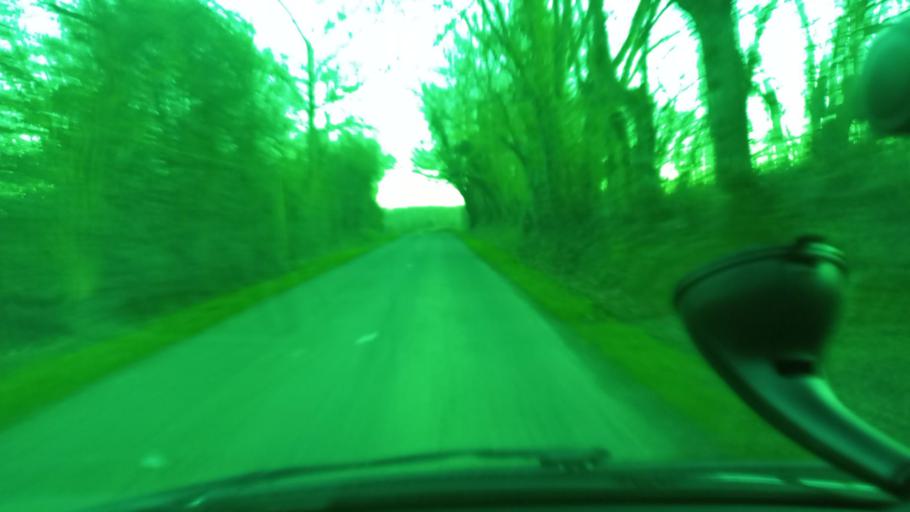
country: FR
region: Pays de la Loire
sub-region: Departement de la Vendee
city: Belleville-sur-Vie
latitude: 46.7911
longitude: -1.4082
